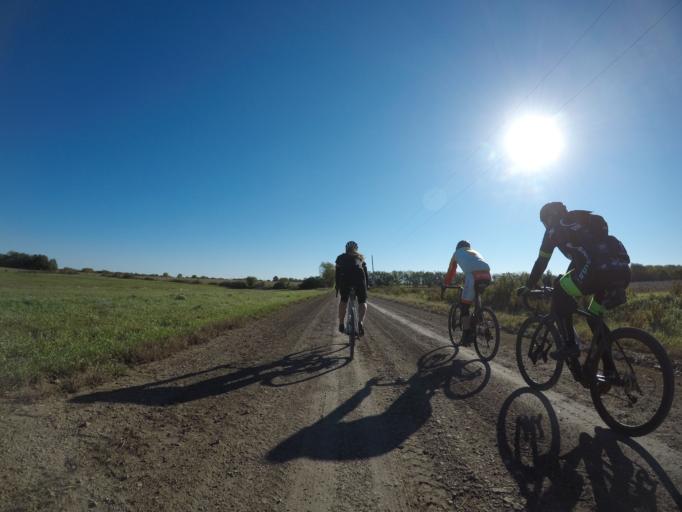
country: US
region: Kansas
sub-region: Morris County
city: Council Grove
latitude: 38.8259
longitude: -96.4567
